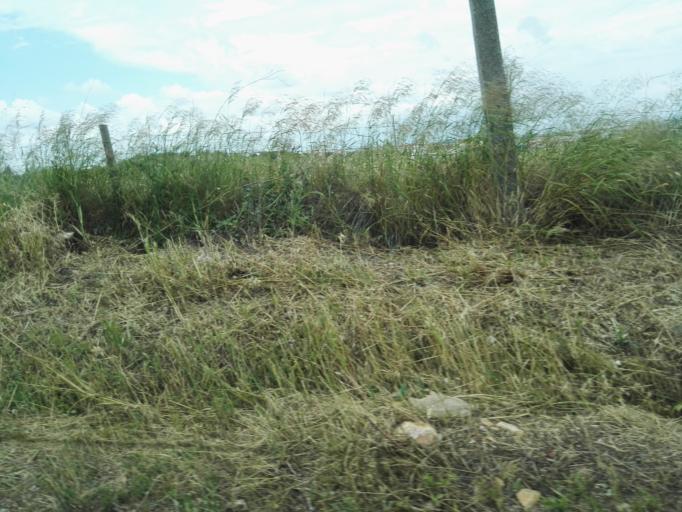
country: PT
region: Portalegre
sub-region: Elvas
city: Elvas
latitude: 38.8739
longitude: -7.1557
